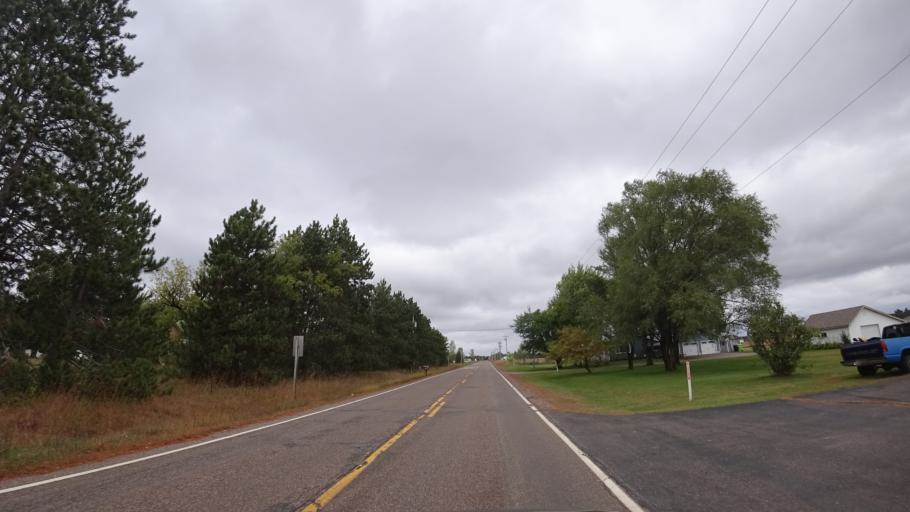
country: US
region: Wisconsin
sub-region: Chippewa County
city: Lake Wissota
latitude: 44.9319
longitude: -91.2677
